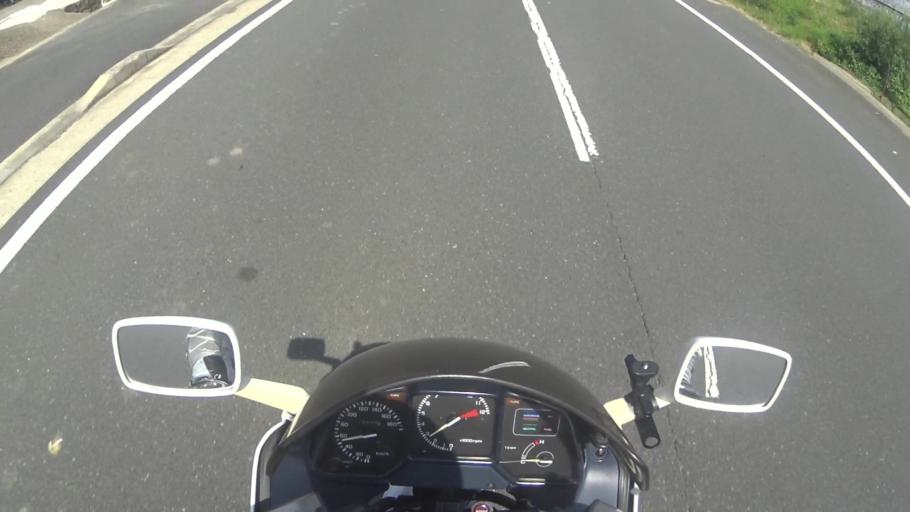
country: JP
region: Kyoto
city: Miyazu
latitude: 35.7307
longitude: 135.2568
